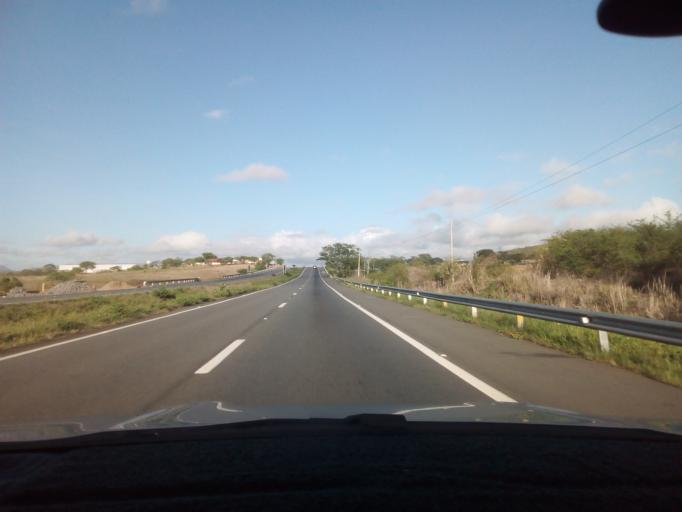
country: BR
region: Paraiba
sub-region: Inga
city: Inga
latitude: -7.2385
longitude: -35.6083
